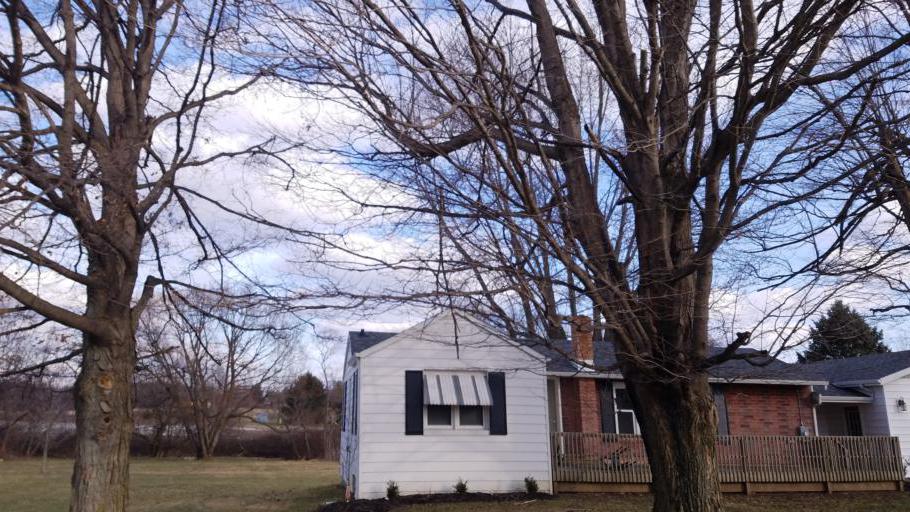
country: US
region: Ohio
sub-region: Crawford County
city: Crestline
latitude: 40.7191
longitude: -82.7033
